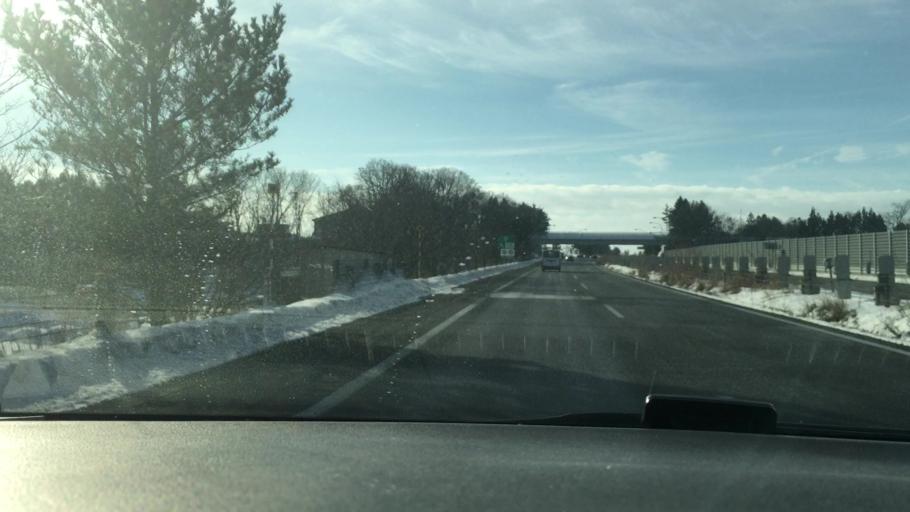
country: JP
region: Iwate
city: Hanamaki
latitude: 39.3736
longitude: 141.0930
